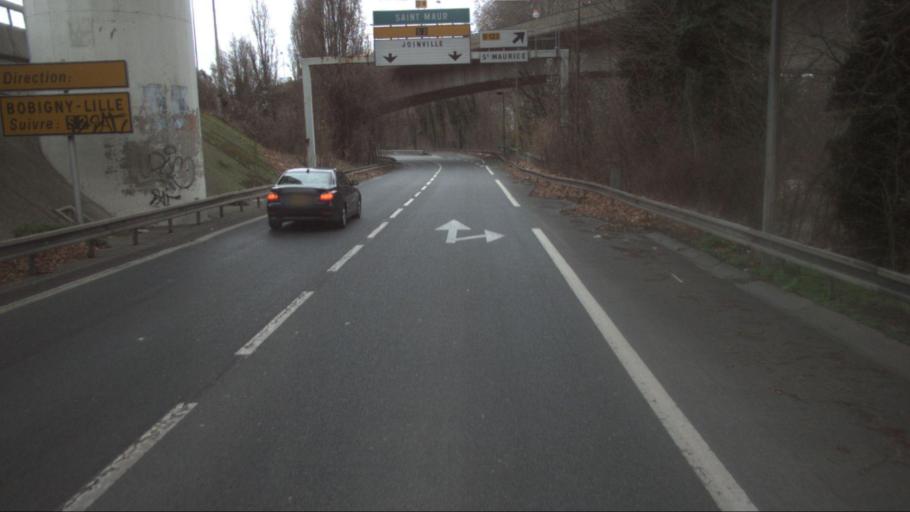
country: FR
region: Ile-de-France
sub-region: Departement du Val-de-Marne
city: Maisons-Alfort
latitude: 48.8162
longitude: 2.4510
